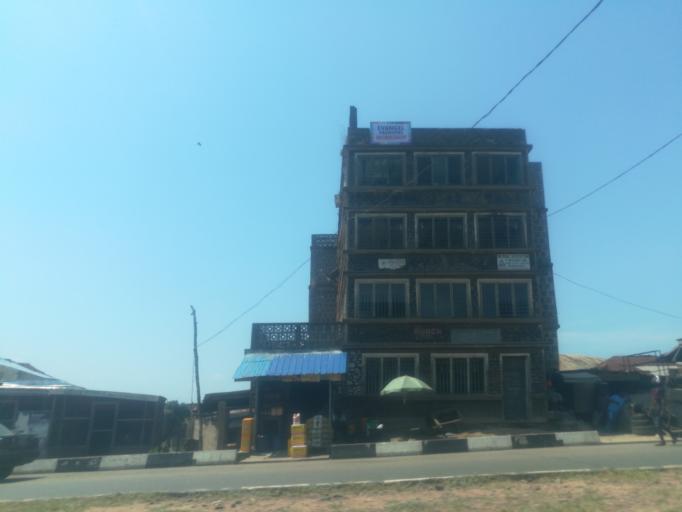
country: NG
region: Ogun
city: Abeokuta
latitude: 7.1593
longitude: 3.3495
